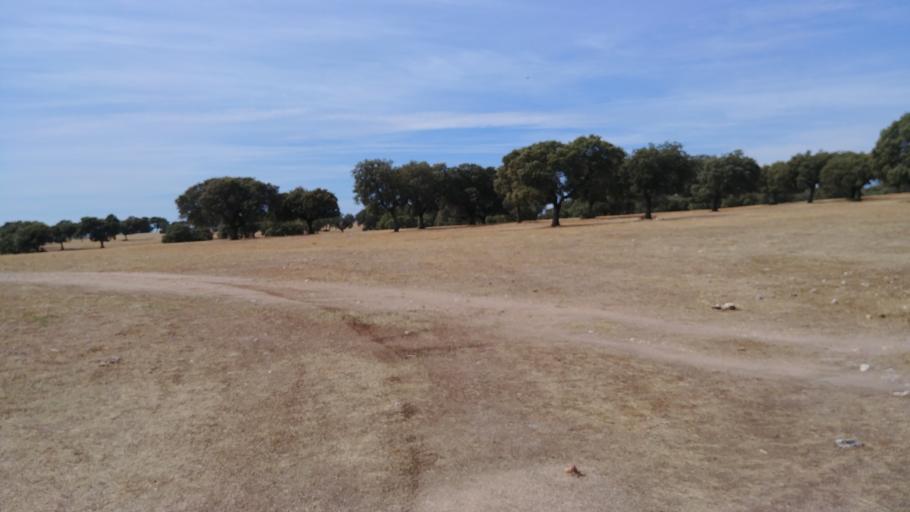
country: ES
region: Castille-La Mancha
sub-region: Province of Toledo
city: Navalcan
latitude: 40.0492
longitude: -5.1189
